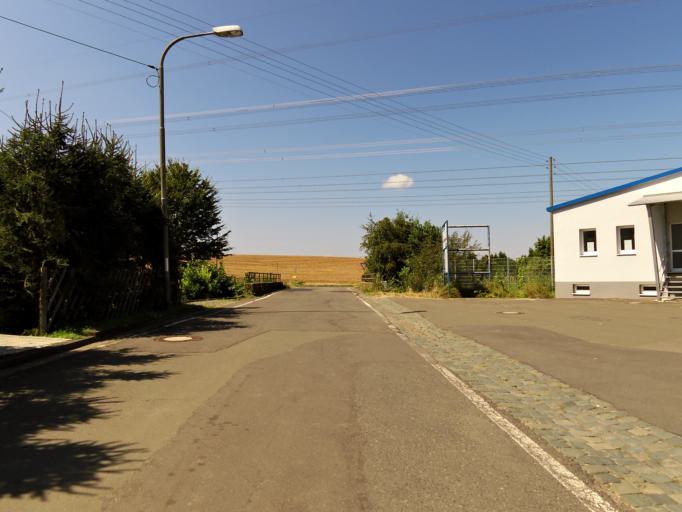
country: DE
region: Rheinland-Pfalz
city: Munchweiler an der Alsenz
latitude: 49.5613
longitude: 7.8862
